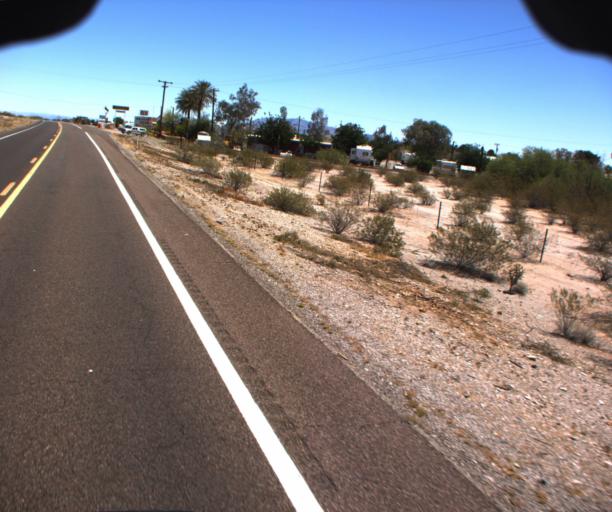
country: US
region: Arizona
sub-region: La Paz County
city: Salome
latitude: 33.7594
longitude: -113.6551
